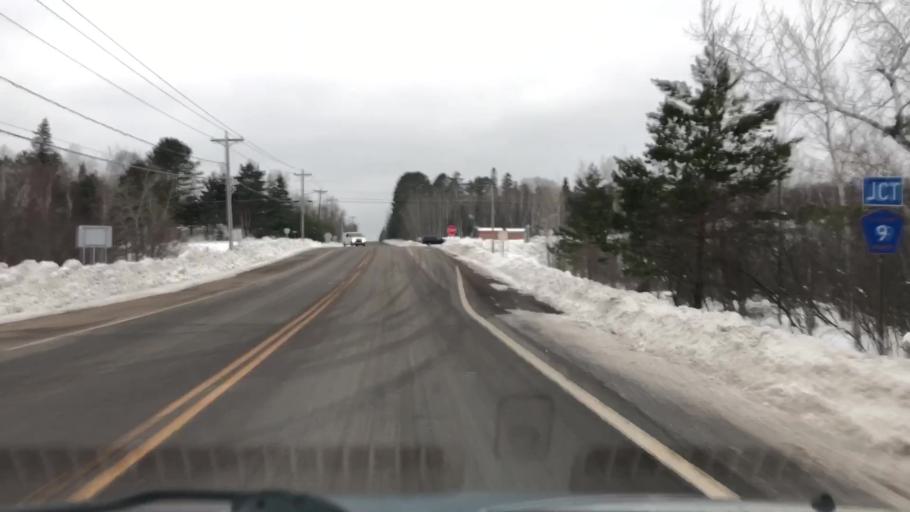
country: US
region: Minnesota
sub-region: Saint Louis County
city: Arnold
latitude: 46.8643
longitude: -92.1111
